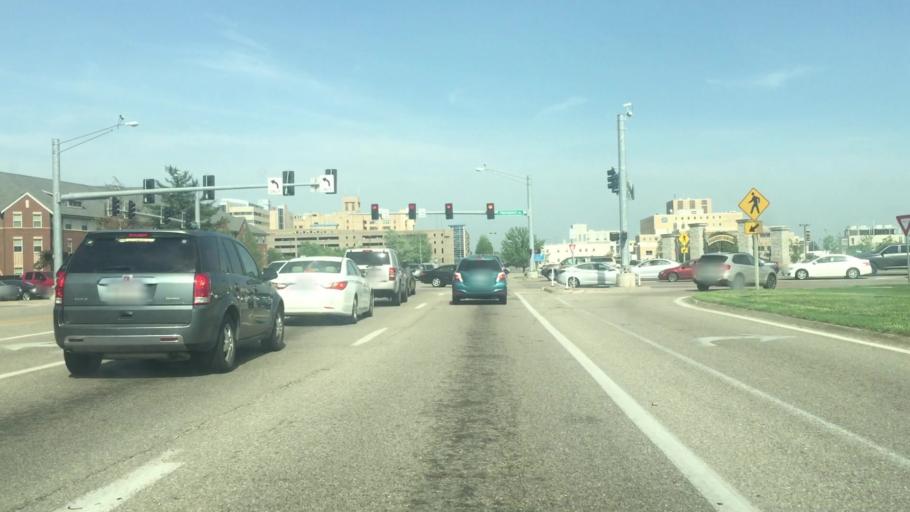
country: US
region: Missouri
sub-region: Boone County
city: Columbia
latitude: 38.9377
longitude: -92.3350
